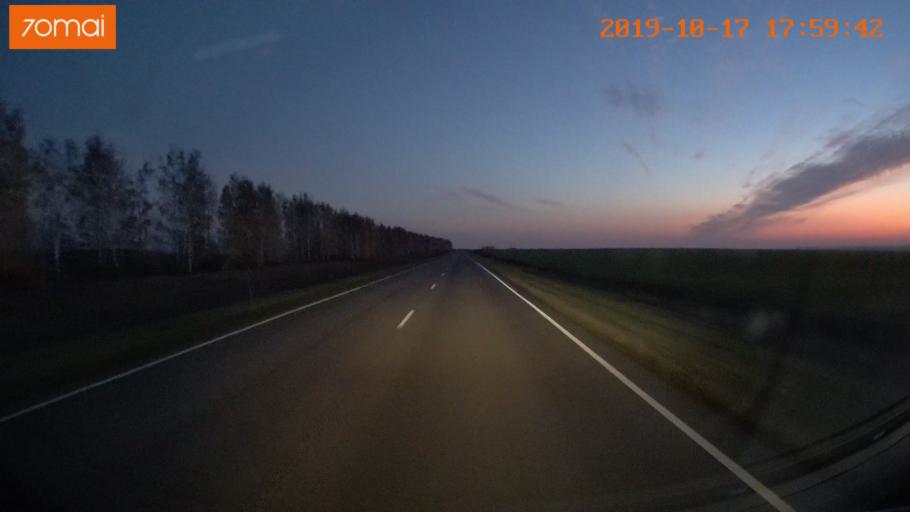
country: RU
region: Tula
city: Kurkino
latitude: 53.5328
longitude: 38.6202
